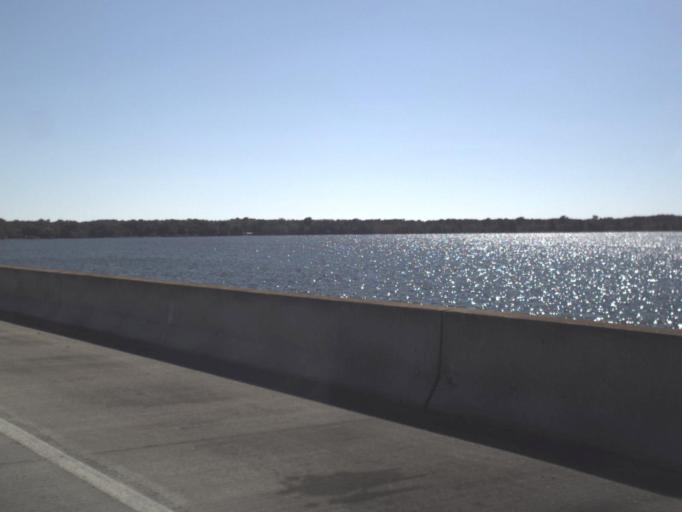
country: US
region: Florida
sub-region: Seminole County
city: Oviedo
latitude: 28.7121
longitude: -81.2393
